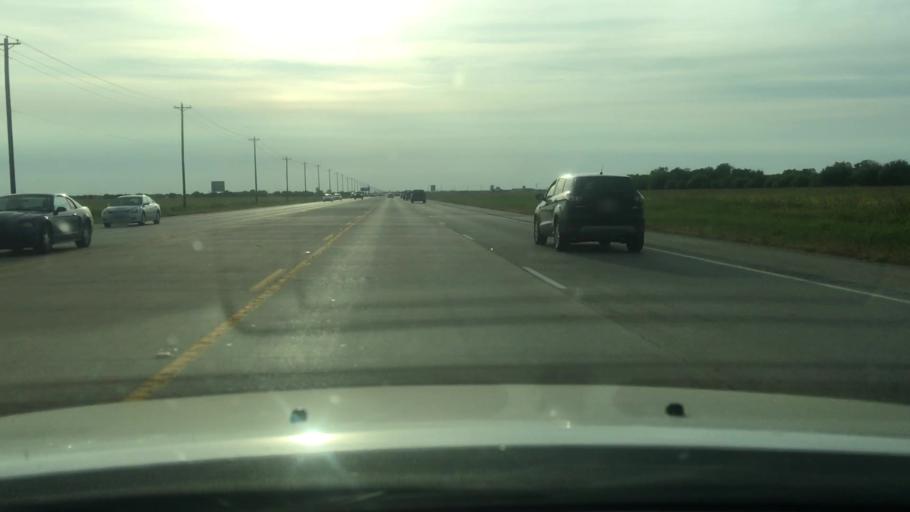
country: US
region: Texas
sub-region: Collin County
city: Prosper
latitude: 33.2194
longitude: -96.8481
